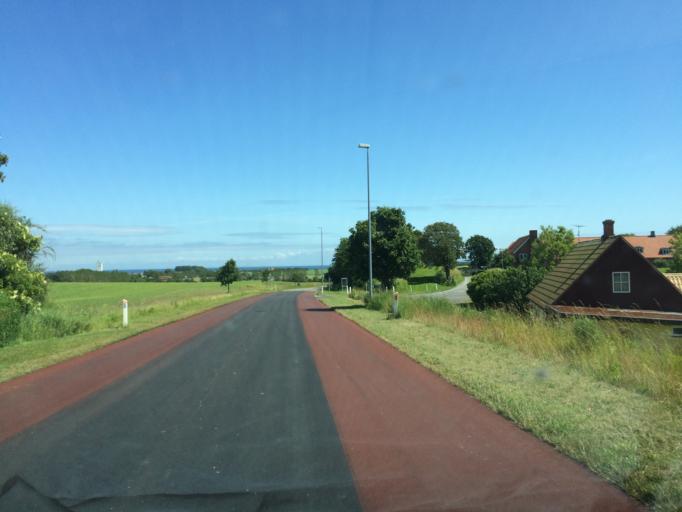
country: DK
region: Central Jutland
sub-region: Samso Kommune
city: Tranebjerg
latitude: 55.8138
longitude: 10.6113
